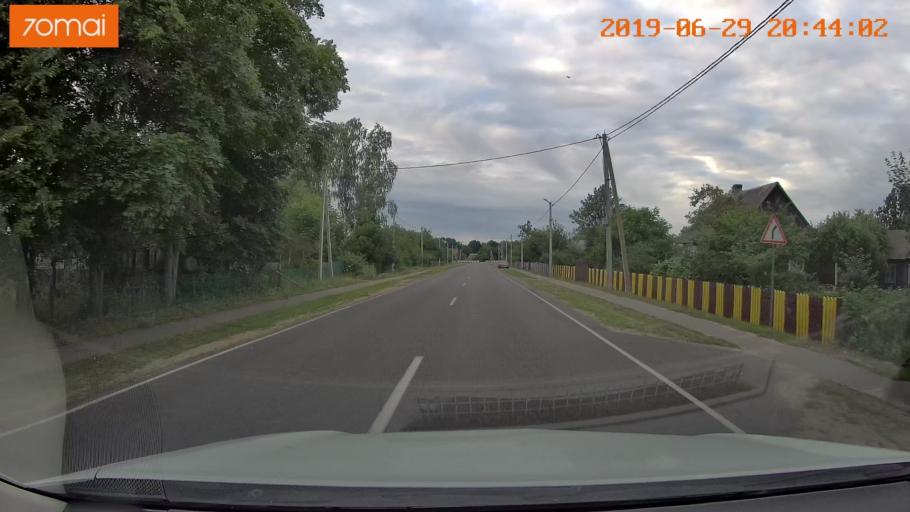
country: BY
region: Brest
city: Hantsavichy
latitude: 52.6100
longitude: 26.3095
